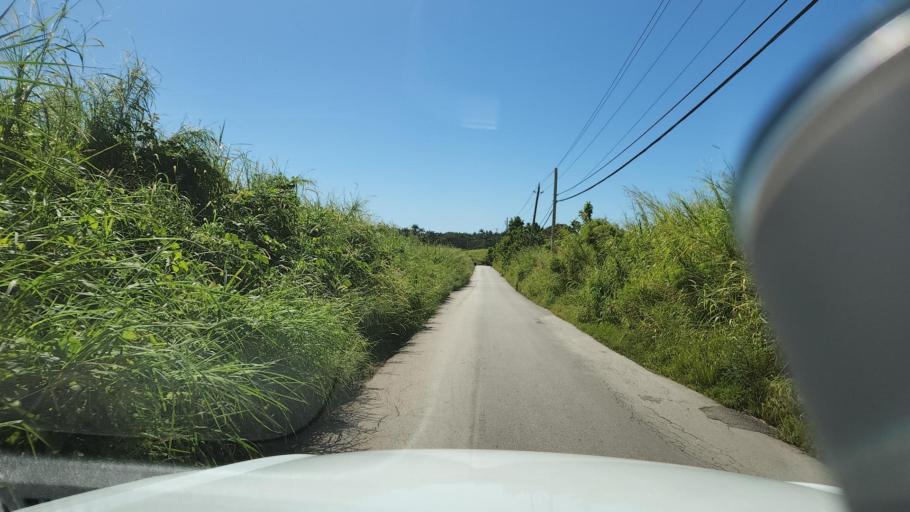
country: BB
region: Saint Thomas
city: Welchman Hall
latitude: 13.1966
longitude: -59.5631
